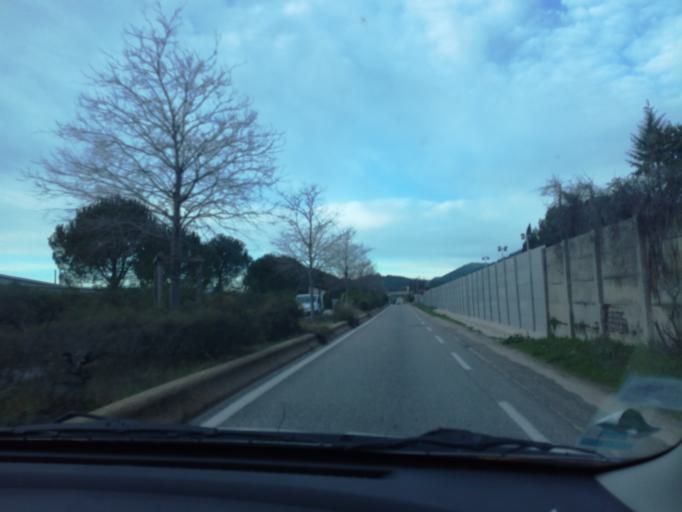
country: FR
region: Provence-Alpes-Cote d'Azur
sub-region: Departement du Var
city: La Farlede
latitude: 43.1606
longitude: 6.0575
